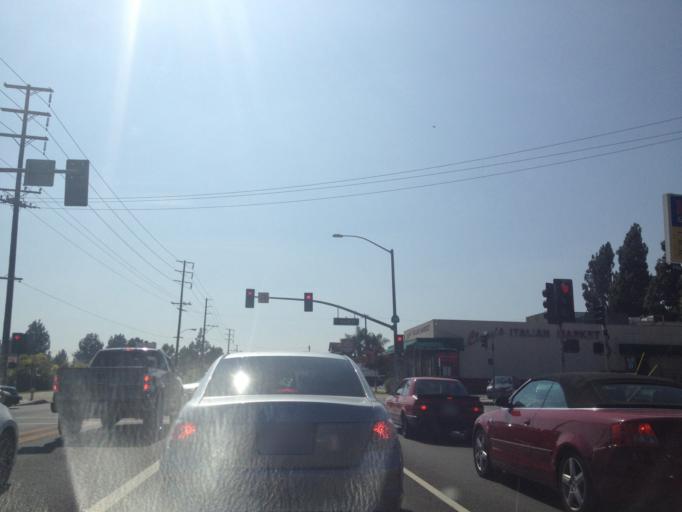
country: US
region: California
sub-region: Orange County
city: La Habra
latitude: 33.9393
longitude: -117.9458
